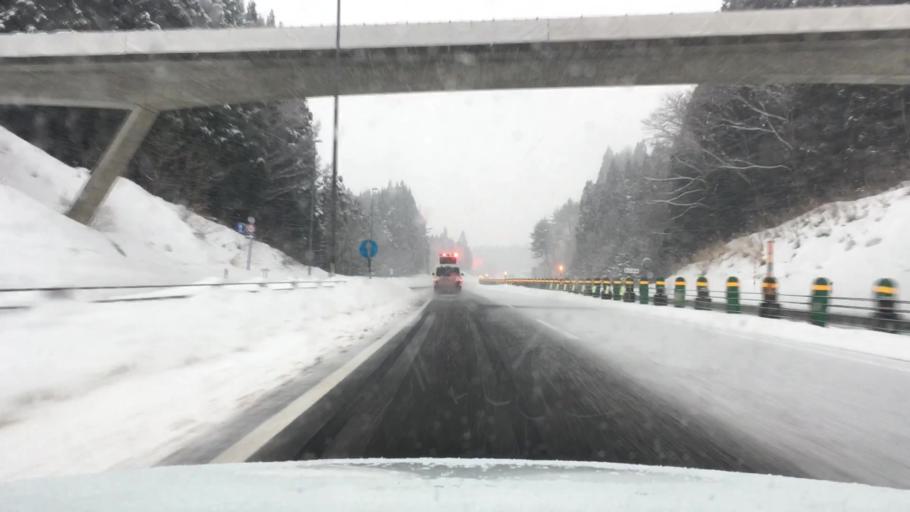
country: JP
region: Akita
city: Hanawa
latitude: 40.1645
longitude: 140.8026
